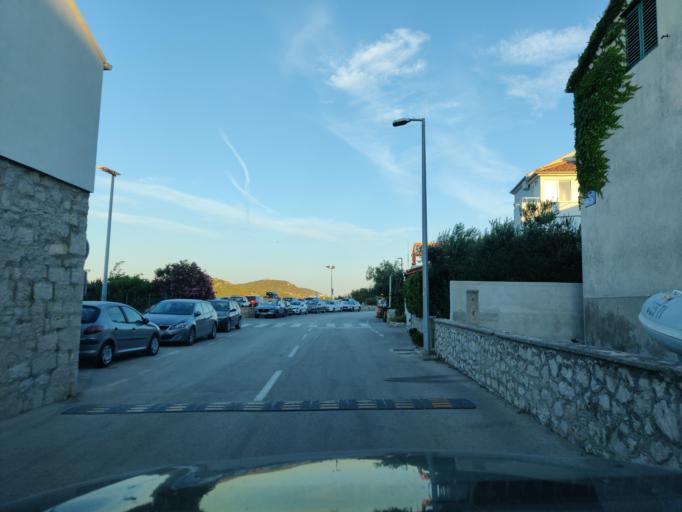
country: HR
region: Sibensko-Kniniska
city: Murter
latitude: 43.8200
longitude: 15.6042
